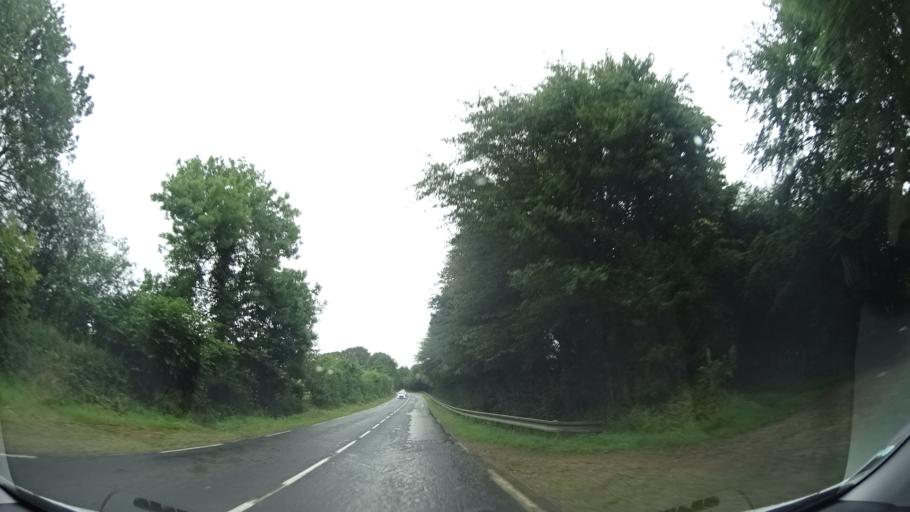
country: FR
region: Lower Normandy
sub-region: Departement de la Manche
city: Martinvast
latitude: 49.6074
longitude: -1.7224
